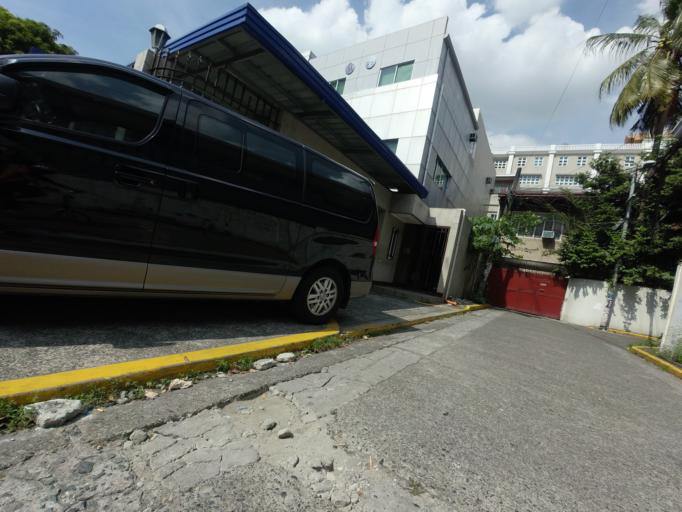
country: PH
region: Metro Manila
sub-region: City of Manila
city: Port Area
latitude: 14.5696
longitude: 120.9935
